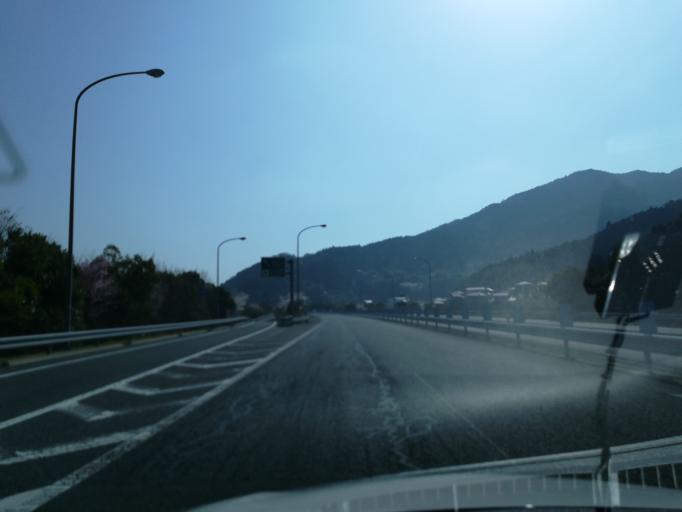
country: JP
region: Tokushima
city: Ikedacho
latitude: 34.0288
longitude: 133.8369
